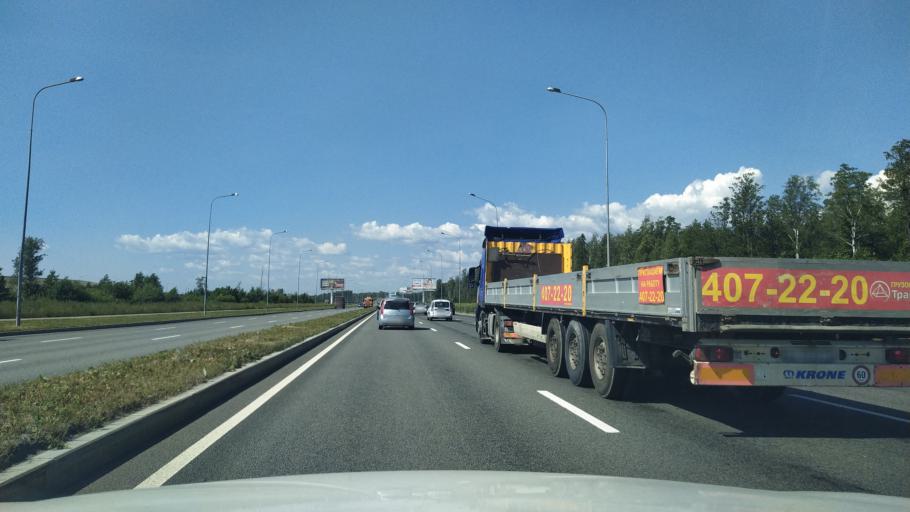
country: RU
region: St.-Petersburg
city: Levashovo
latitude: 60.0665
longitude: 30.1904
